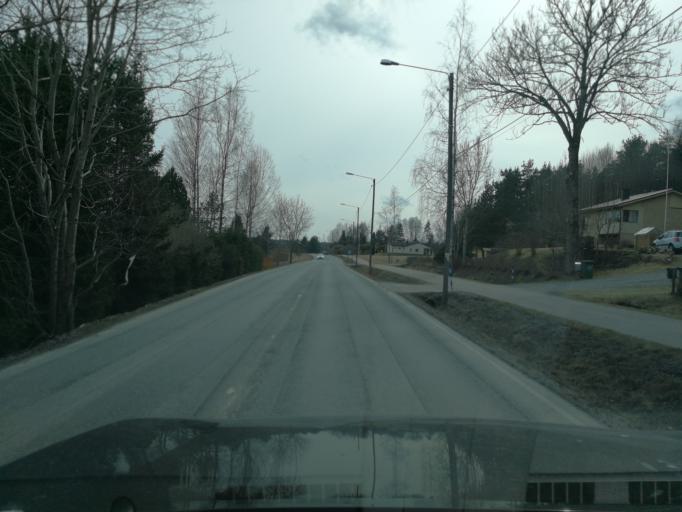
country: FI
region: Uusimaa
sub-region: Helsinki
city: Lohja
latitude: 60.2052
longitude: 24.0096
